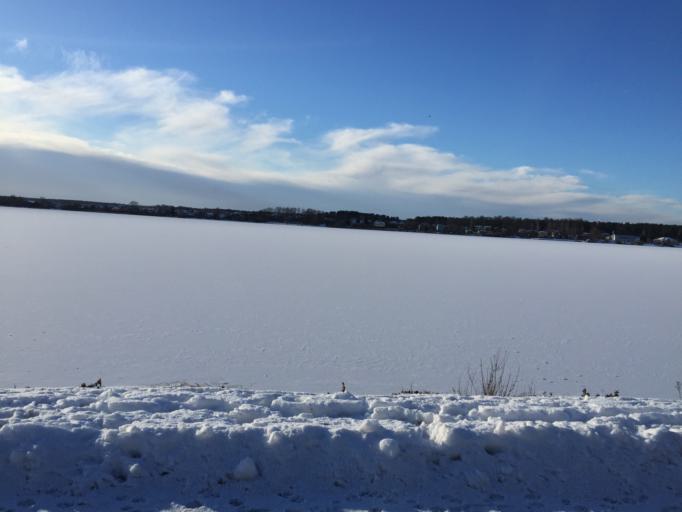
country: LV
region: Kekava
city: Balozi
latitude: 56.9033
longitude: 24.1883
